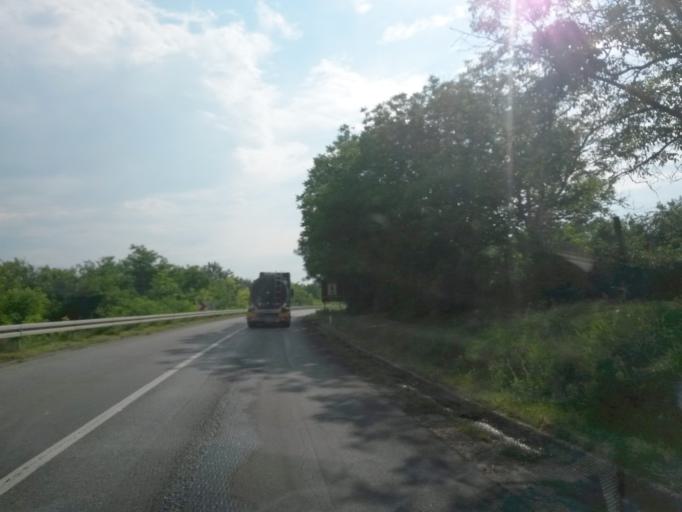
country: RS
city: Bogojevo
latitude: 45.5102
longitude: 19.0738
